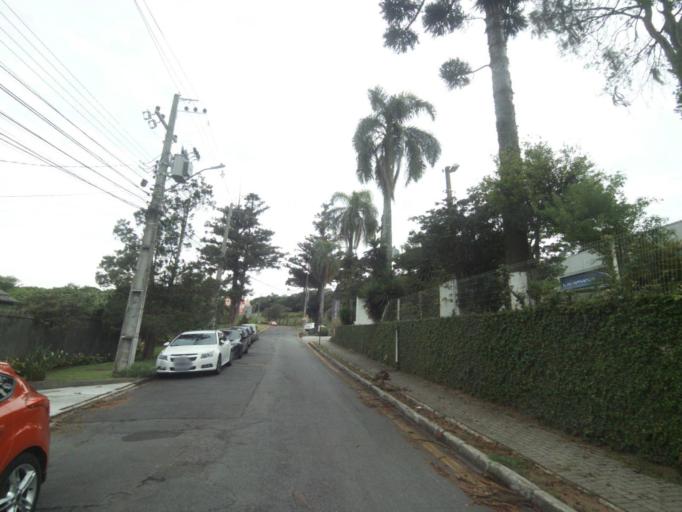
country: BR
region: Parana
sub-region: Curitiba
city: Curitiba
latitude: -25.4138
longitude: -49.3057
